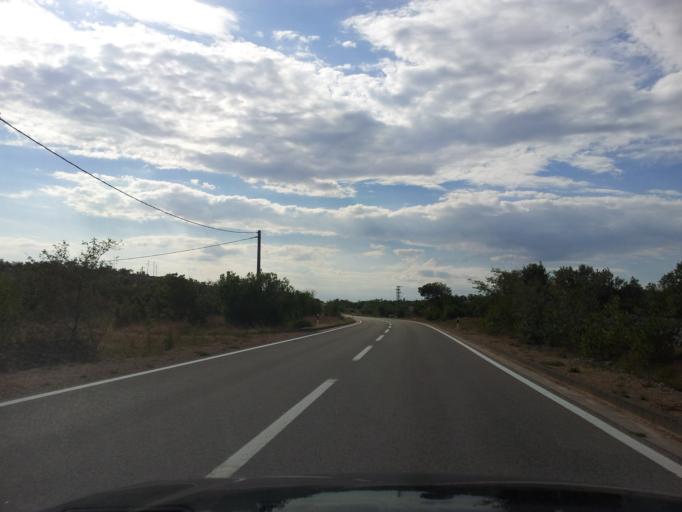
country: HR
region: Zadarska
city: Pridraga
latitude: 44.2321
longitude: 15.5712
